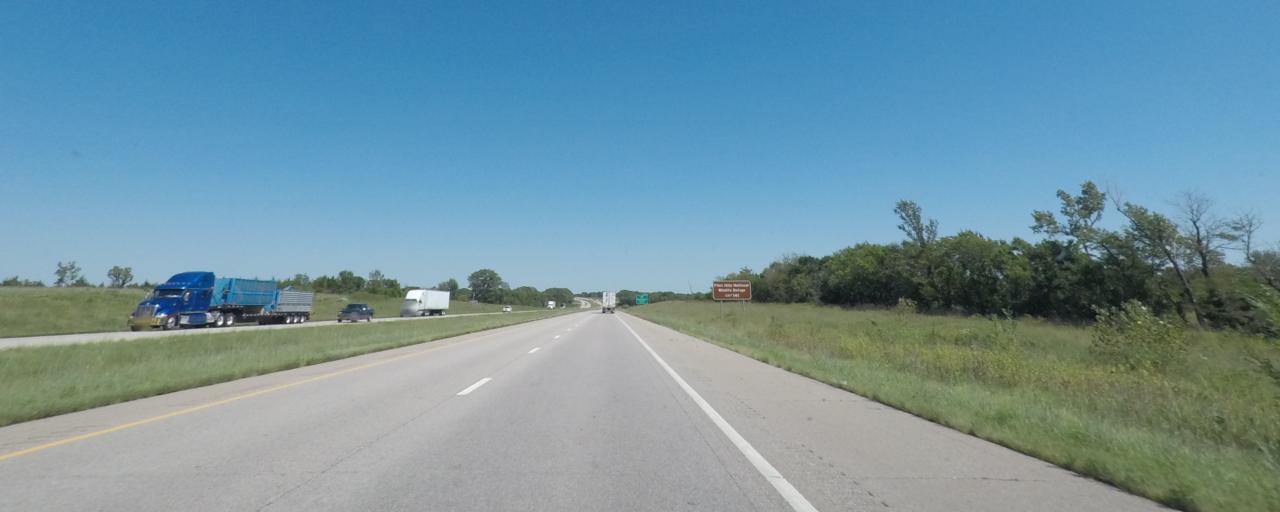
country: US
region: Kansas
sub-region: Lyon County
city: Emporia
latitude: 38.4092
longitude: -96.0047
